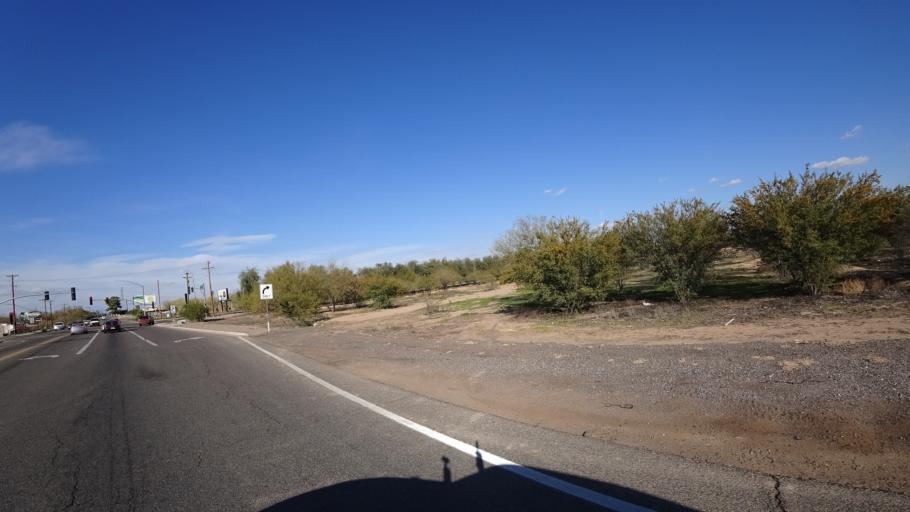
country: US
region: Arizona
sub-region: Maricopa County
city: Peoria
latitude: 33.5511
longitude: -112.2378
